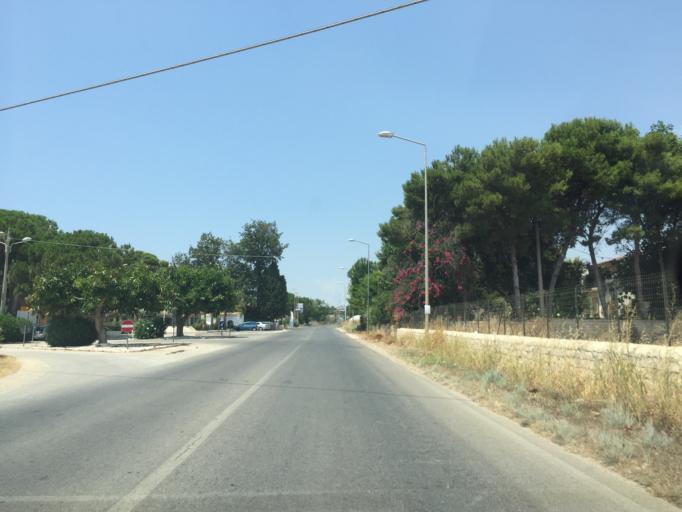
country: IT
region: Sicily
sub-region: Ragusa
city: Donnalucata
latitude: 36.7713
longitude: 14.6104
